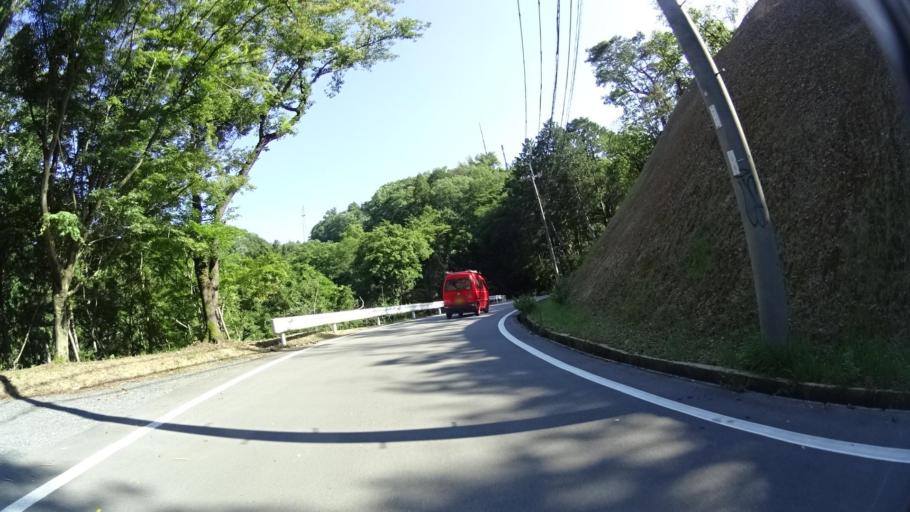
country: JP
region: Kyoto
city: Kameoka
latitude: 34.9945
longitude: 135.5620
